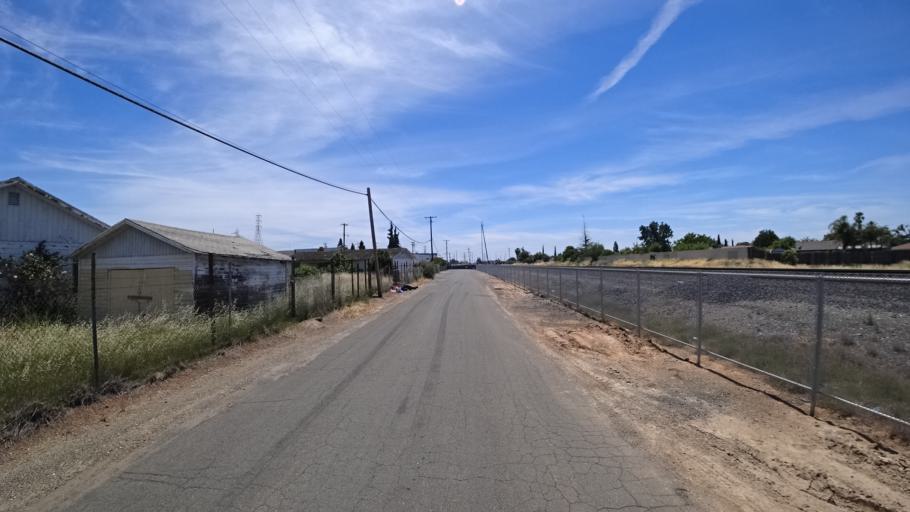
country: US
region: California
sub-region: Sacramento County
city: Florin
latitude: 38.5346
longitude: -121.4109
